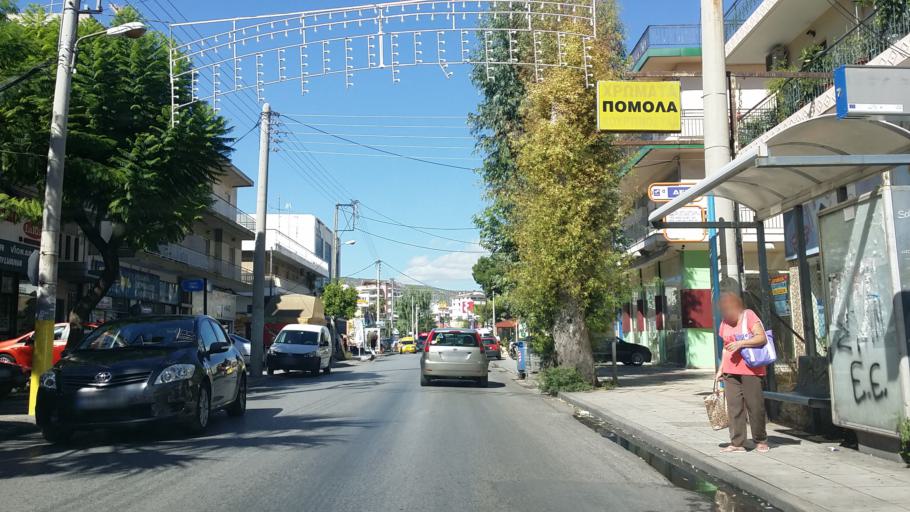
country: GR
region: Attica
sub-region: Nomarchia Athinas
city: Agioi Anargyroi
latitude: 38.0295
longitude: 23.7148
